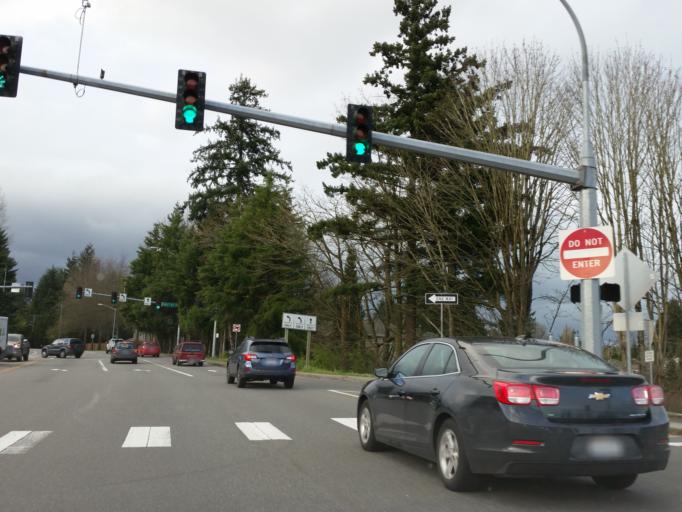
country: US
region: Washington
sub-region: King County
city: Woodinville
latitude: 47.7588
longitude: -122.1637
